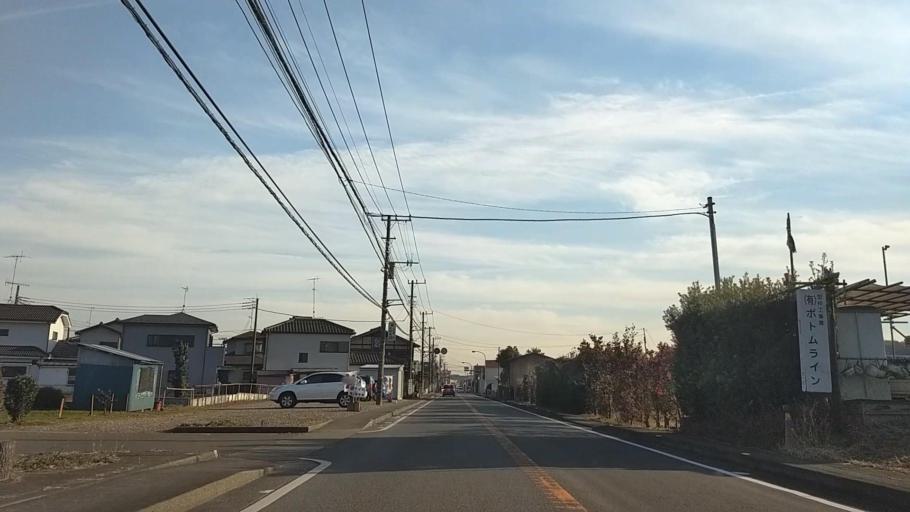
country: JP
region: Kanagawa
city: Zama
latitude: 35.5013
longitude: 139.3121
